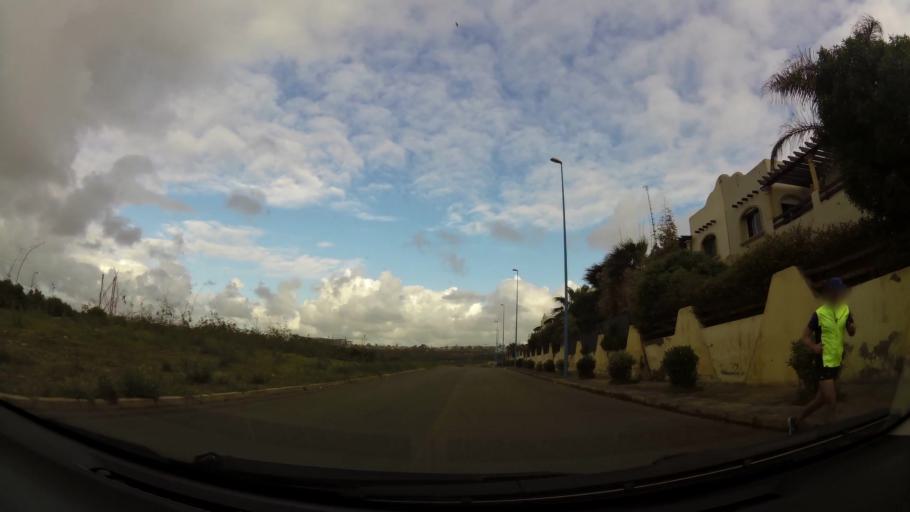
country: MA
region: Grand Casablanca
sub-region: Casablanca
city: Casablanca
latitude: 33.5792
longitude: -7.6937
